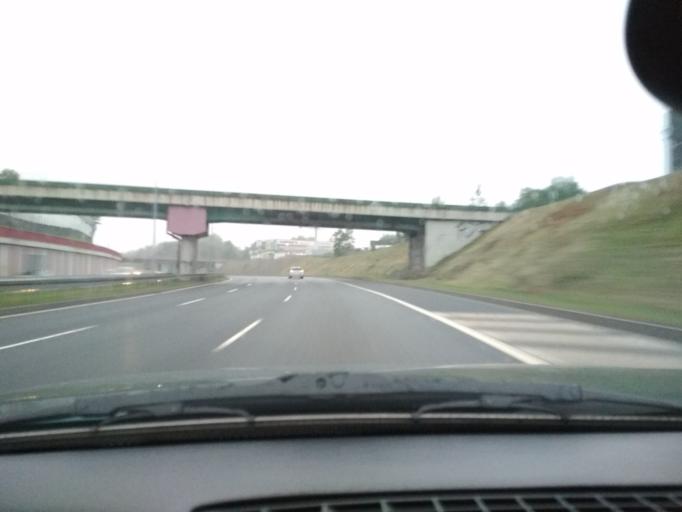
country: PL
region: Silesian Voivodeship
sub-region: Swietochlowice
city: Swietochlowice
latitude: 50.3001
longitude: 18.8792
